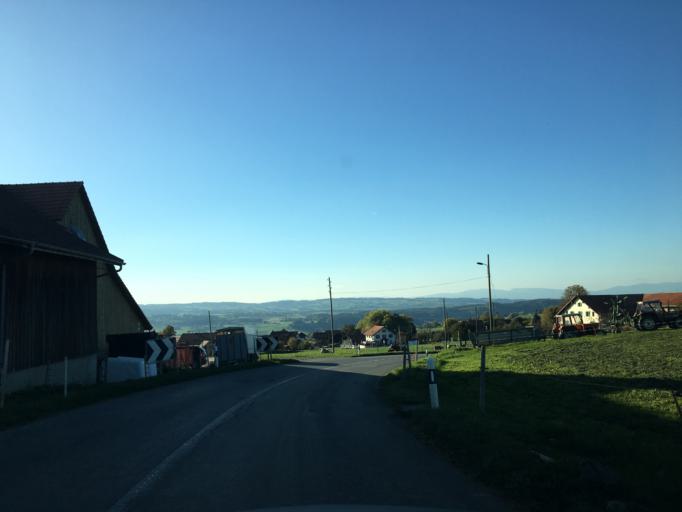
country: CH
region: Vaud
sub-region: Lavaux-Oron District
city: Oron-la-ville
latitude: 46.5757
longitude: 6.8580
